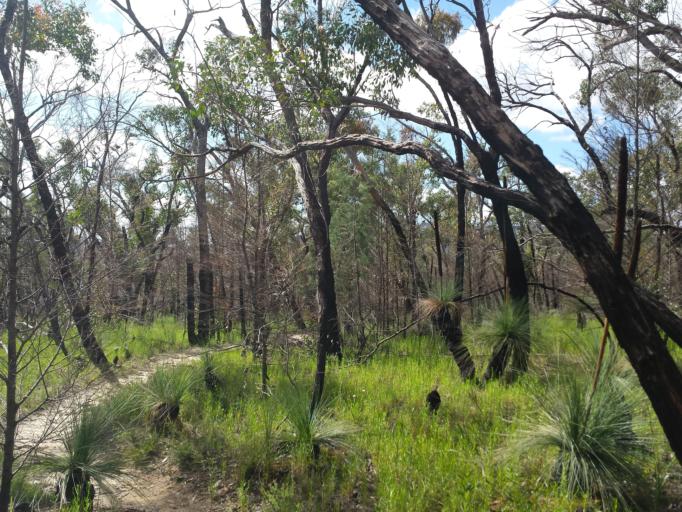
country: AU
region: Victoria
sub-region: Southern Grampians
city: Hamilton
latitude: -37.2714
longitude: 142.2733
